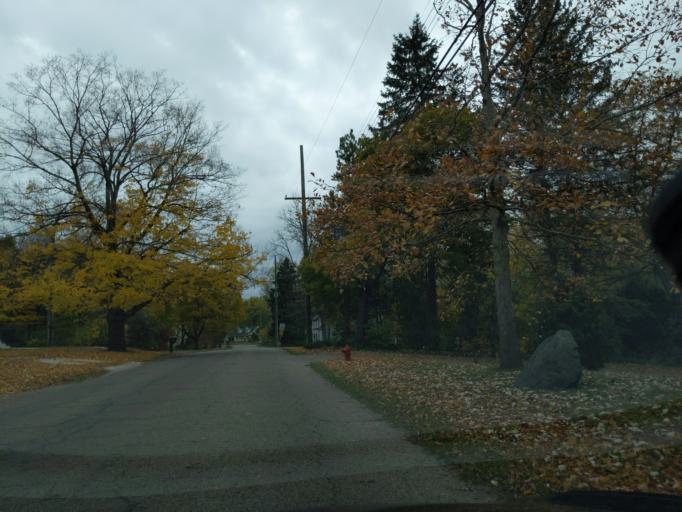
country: US
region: Michigan
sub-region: Eaton County
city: Eaton Rapids
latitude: 42.5170
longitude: -84.6490
